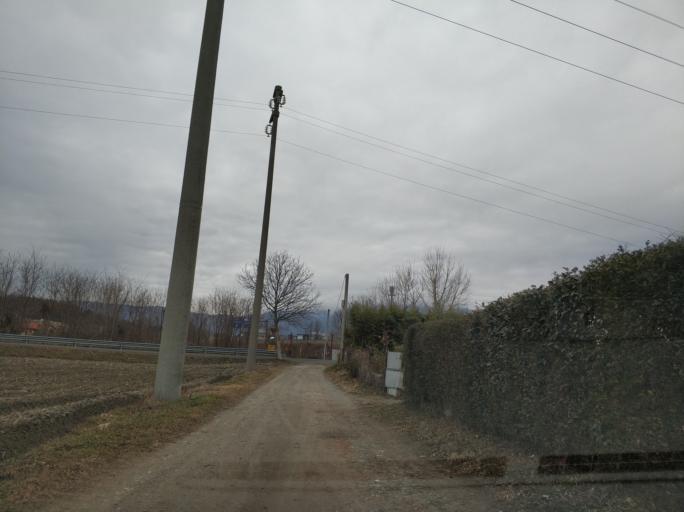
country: IT
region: Piedmont
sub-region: Provincia di Torino
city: Ivrea
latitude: 45.4555
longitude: 7.8876
